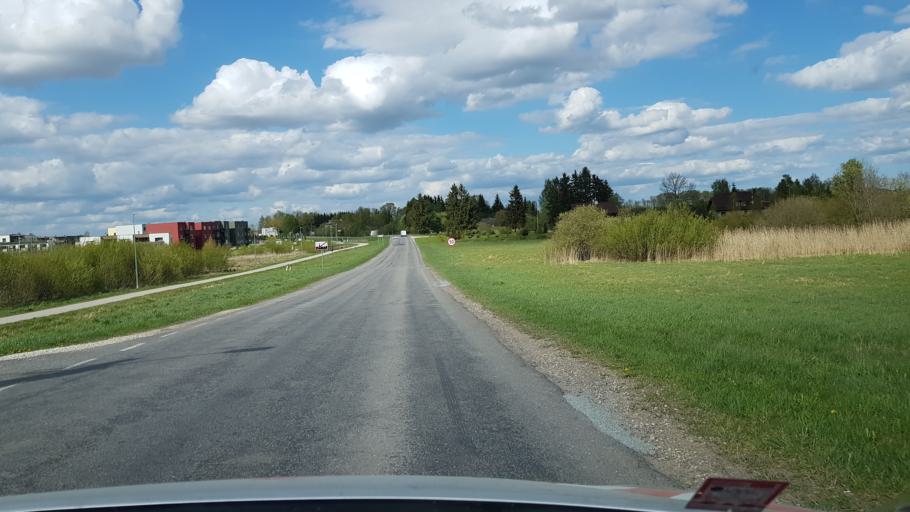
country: EE
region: Tartu
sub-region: Tartu linn
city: Tartu
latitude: 58.3619
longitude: 26.7971
